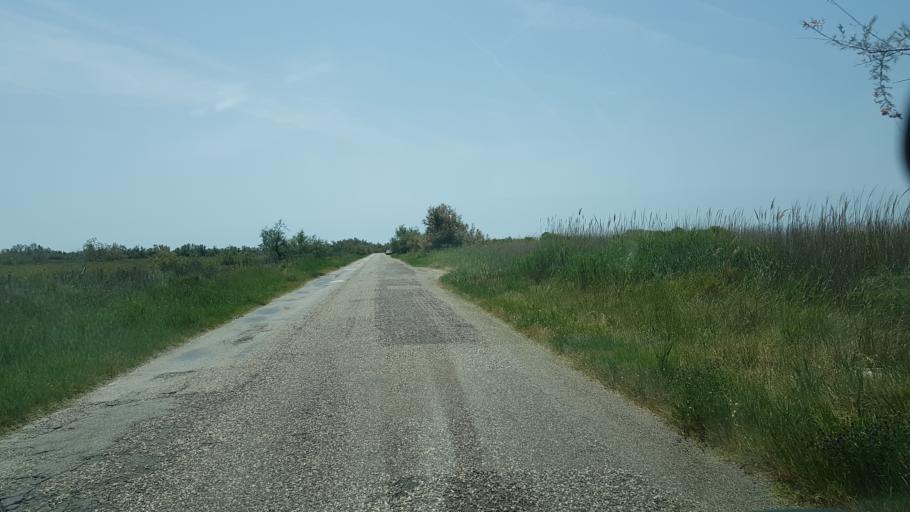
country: FR
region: Provence-Alpes-Cote d'Azur
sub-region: Departement des Bouches-du-Rhone
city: Arles
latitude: 43.5526
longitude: 4.6274
